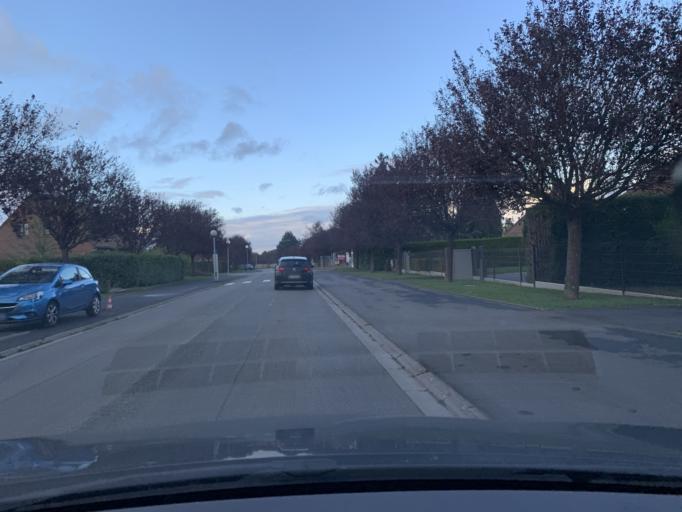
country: FR
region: Nord-Pas-de-Calais
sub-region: Departement du Nord
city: Proville
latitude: 50.1546
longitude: 3.2109
